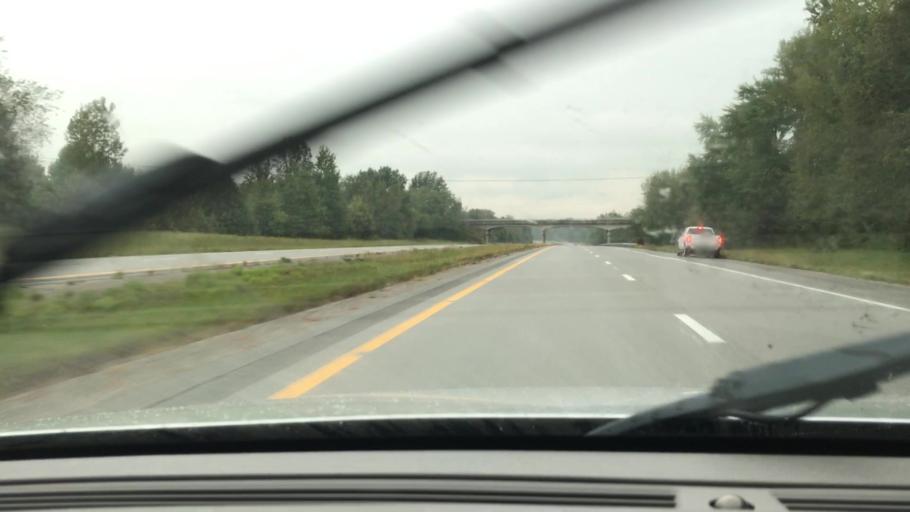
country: US
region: Kentucky
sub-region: Barren County
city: Glasgow
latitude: 37.0206
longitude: -86.0364
